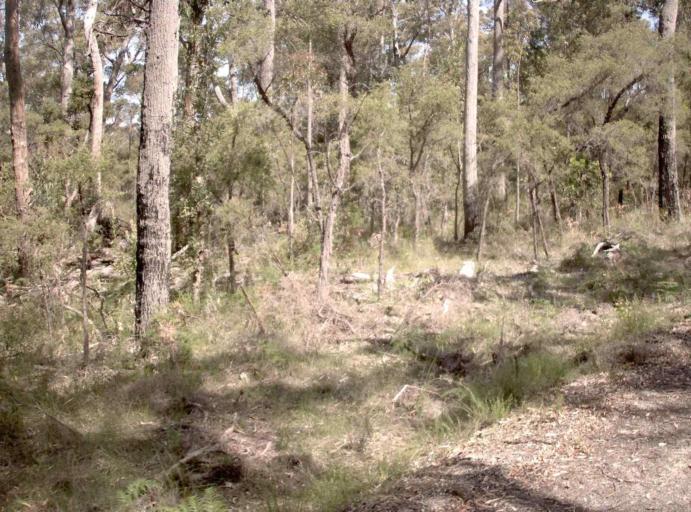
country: AU
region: New South Wales
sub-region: Bega Valley
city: Eden
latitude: -37.5368
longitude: 149.6970
